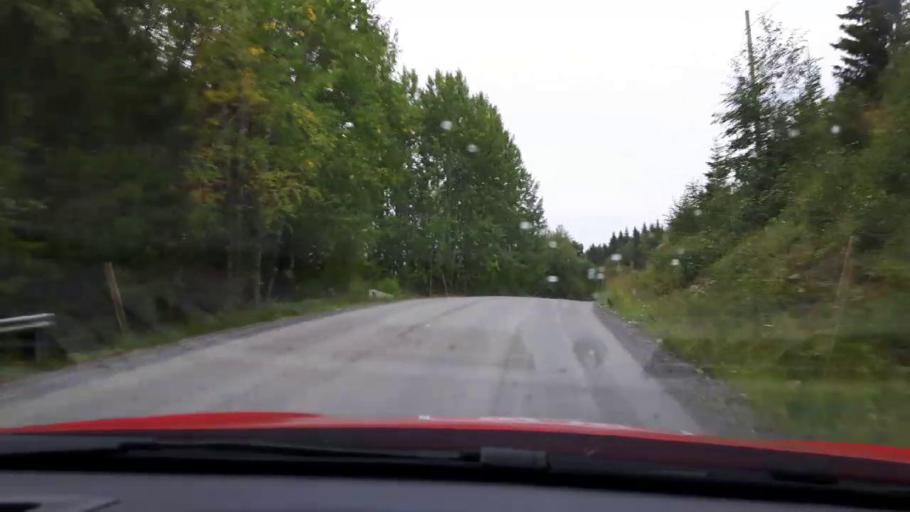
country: SE
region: Jaemtland
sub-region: Are Kommun
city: Jarpen
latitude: 63.4103
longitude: 13.3580
